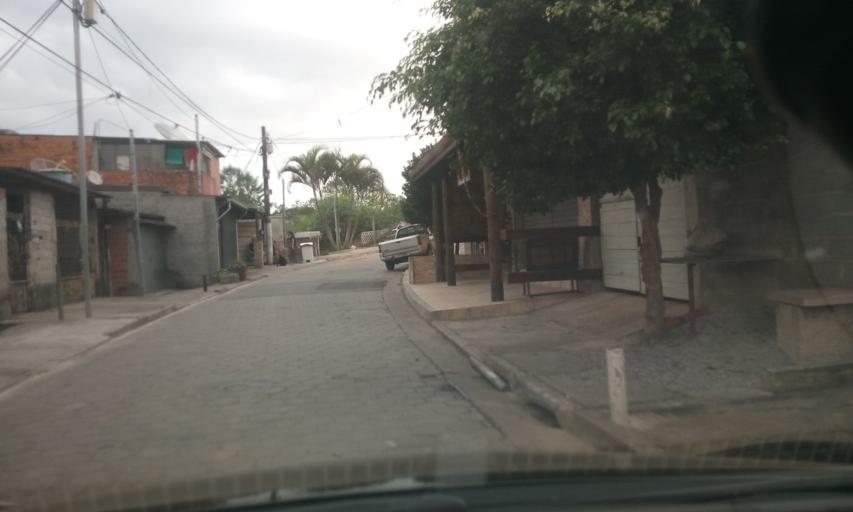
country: BR
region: Sao Paulo
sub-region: Diadema
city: Diadema
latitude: -23.7716
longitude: -46.6094
